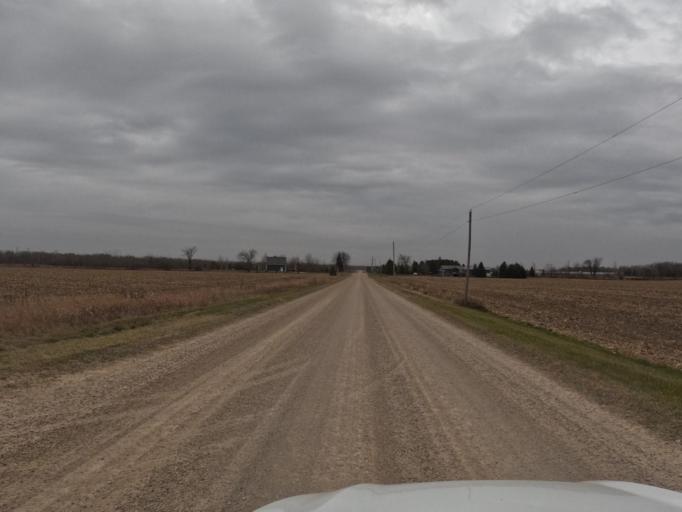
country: CA
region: Ontario
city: Shelburne
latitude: 43.8806
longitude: -80.3579
